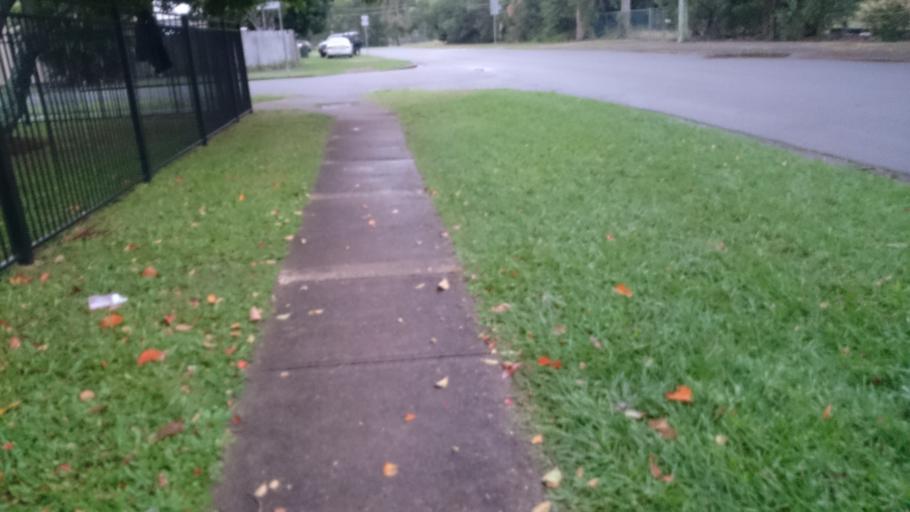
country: AU
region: Queensland
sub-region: Brisbane
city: Manly West
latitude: -27.4689
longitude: 153.1881
